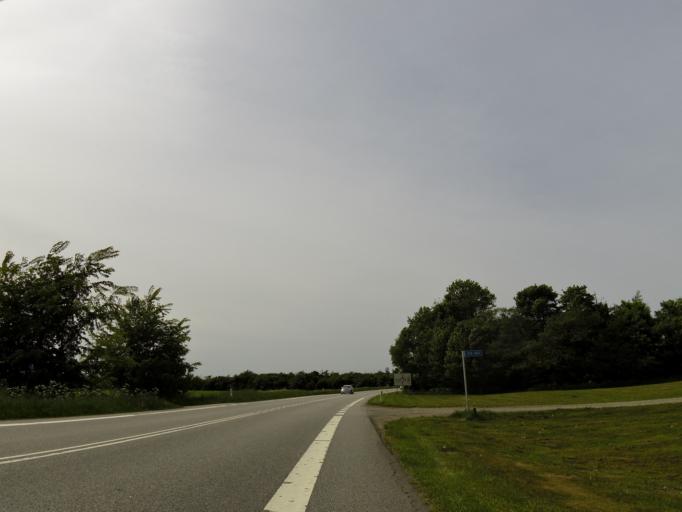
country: DK
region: Central Jutland
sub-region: Holstebro Kommune
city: Vinderup
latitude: 56.5685
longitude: 8.8778
